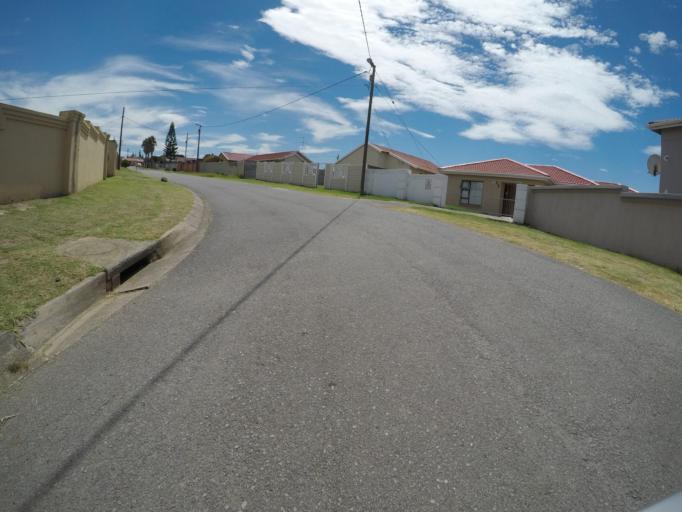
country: ZA
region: Eastern Cape
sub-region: Buffalo City Metropolitan Municipality
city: East London
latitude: -33.0423
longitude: 27.8646
